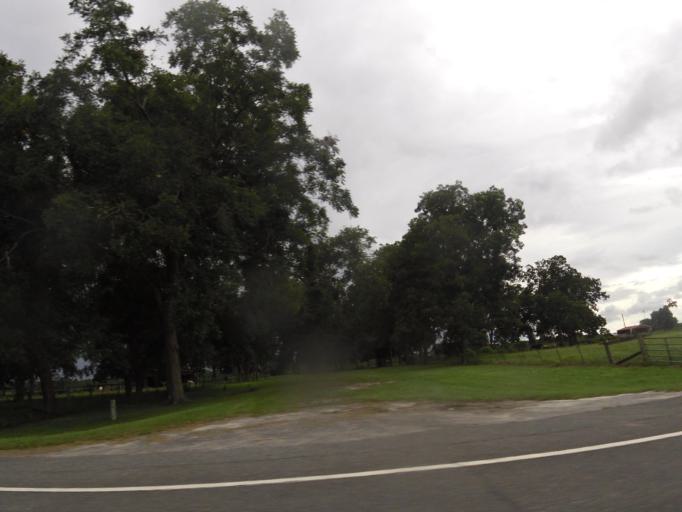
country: US
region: Florida
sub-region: Baker County
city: Macclenny
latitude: 30.4199
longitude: -82.2002
